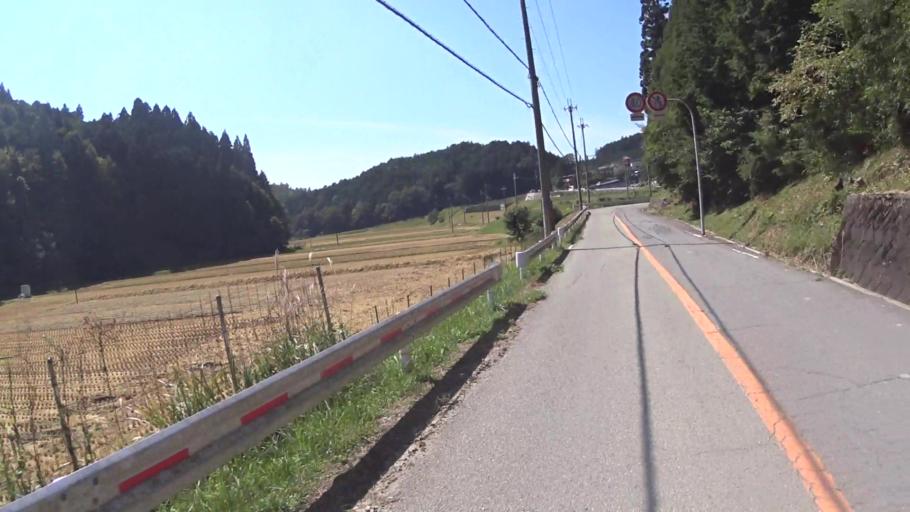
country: JP
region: Kyoto
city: Kameoka
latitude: 34.9623
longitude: 135.6013
